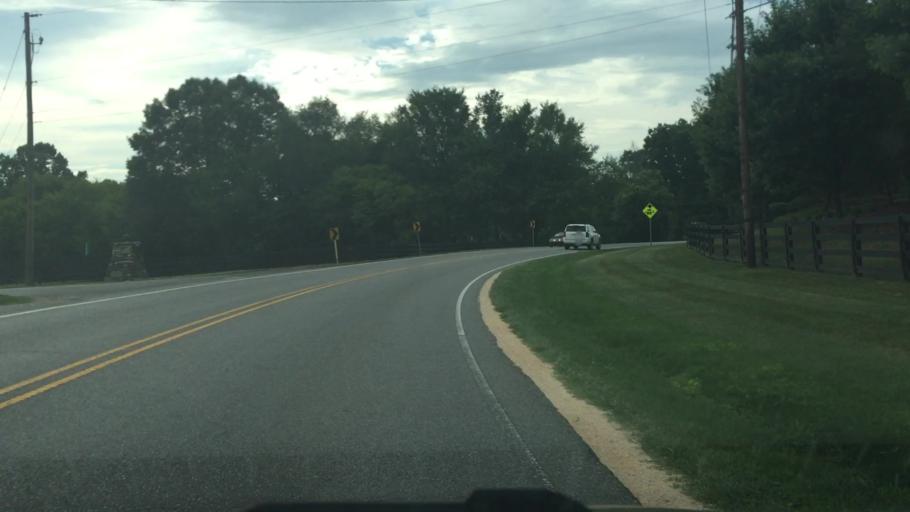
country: US
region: North Carolina
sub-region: Rowan County
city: Enochville
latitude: 35.4305
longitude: -80.7230
